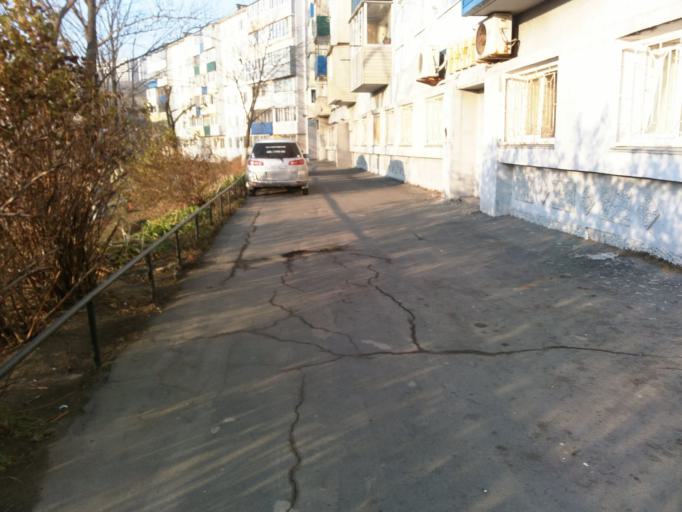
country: RU
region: Primorskiy
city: Vladivostok
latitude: 43.0899
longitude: 131.9744
